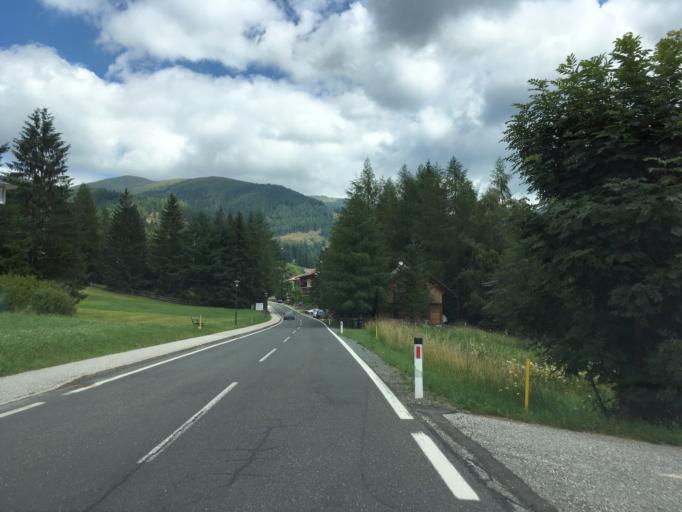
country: AT
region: Carinthia
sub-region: Politischer Bezirk Spittal an der Drau
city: Kleinkirchheim
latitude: 46.8392
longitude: 13.7651
